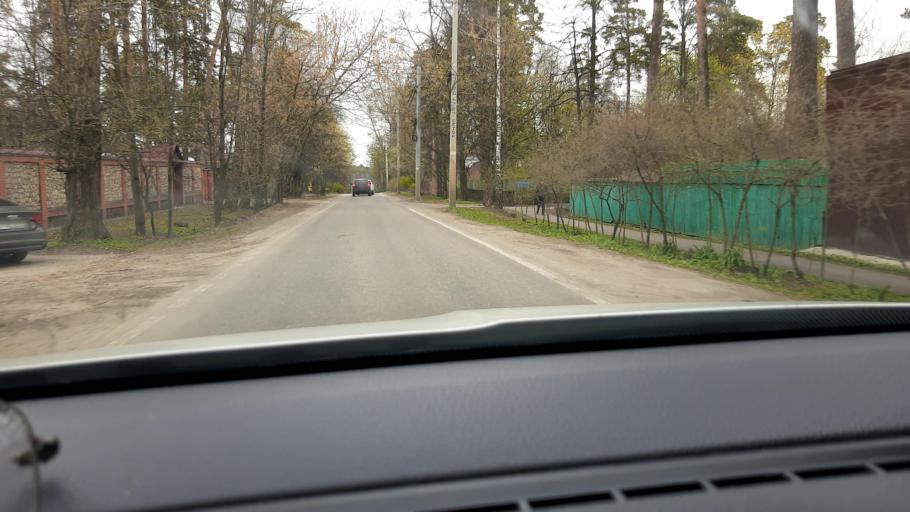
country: RU
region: Moskovskaya
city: Vidnoye
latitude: 55.5465
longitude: 37.6801
